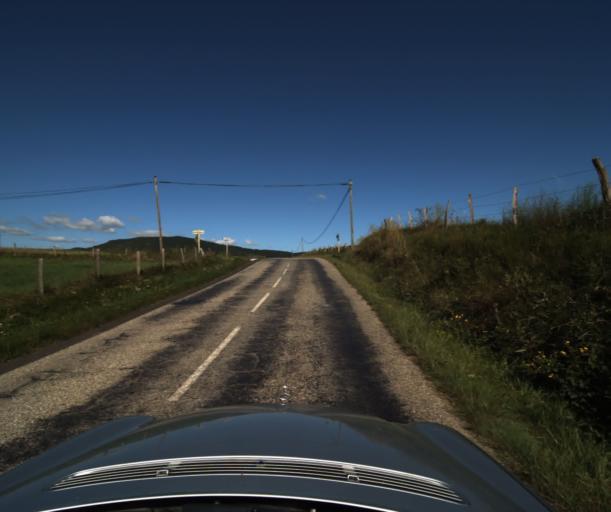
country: FR
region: Midi-Pyrenees
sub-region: Departement de l'Ariege
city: Lavelanet
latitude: 42.9925
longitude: 1.8892
